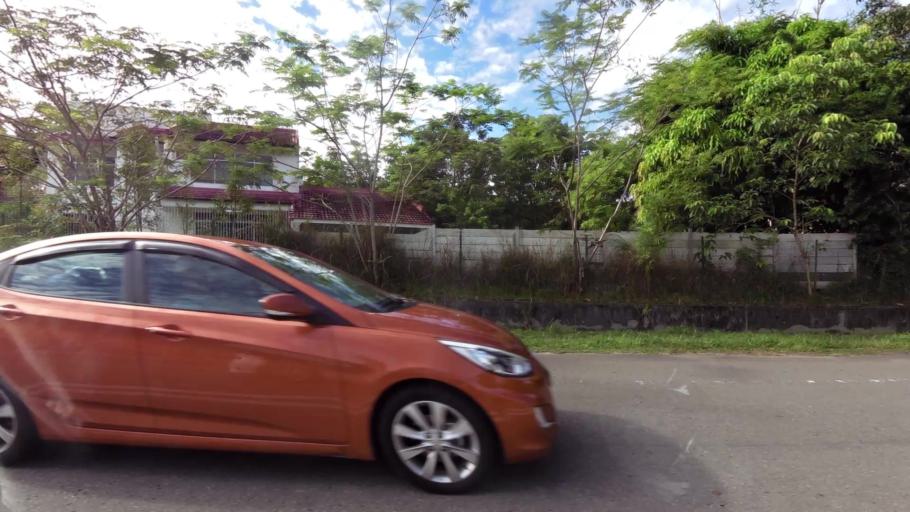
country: BN
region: Brunei and Muara
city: Bandar Seri Begawan
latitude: 4.8949
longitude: 114.9672
